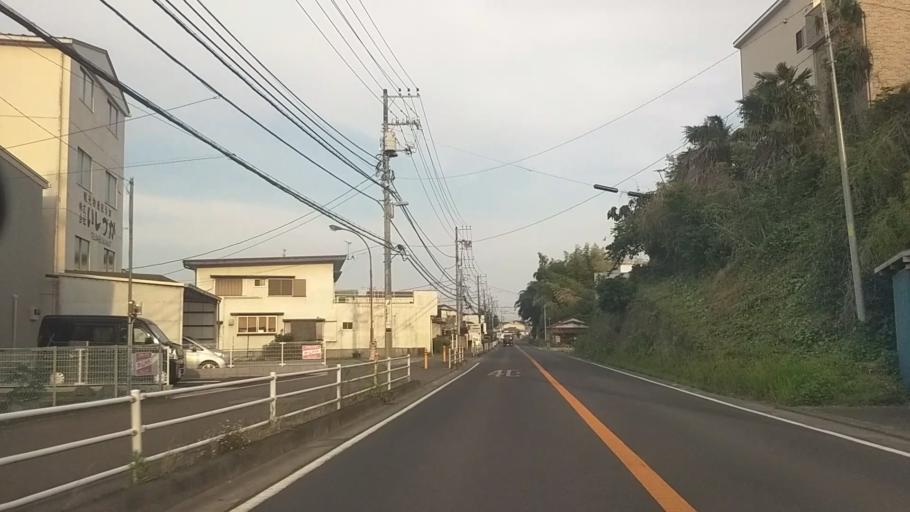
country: JP
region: Kanagawa
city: Odawara
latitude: 35.2824
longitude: 139.1446
